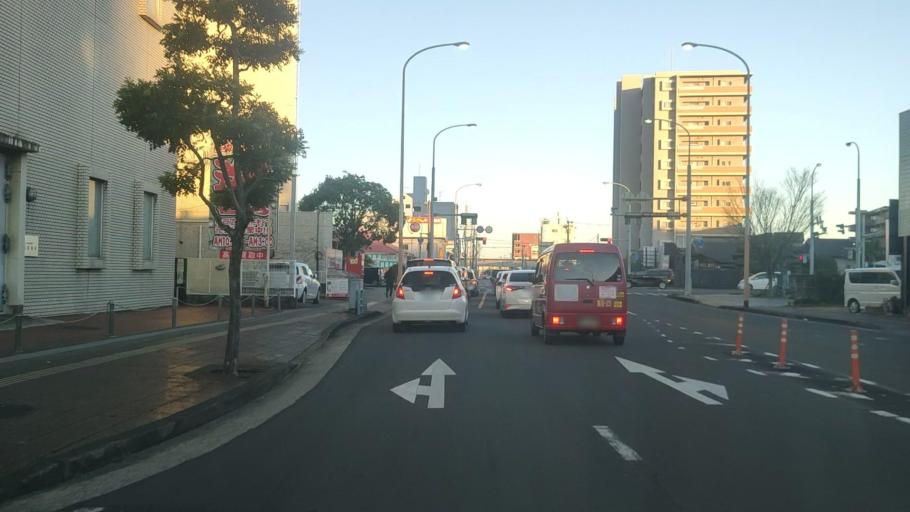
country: JP
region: Miyazaki
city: Miyazaki-shi
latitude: 31.9080
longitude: 131.4279
